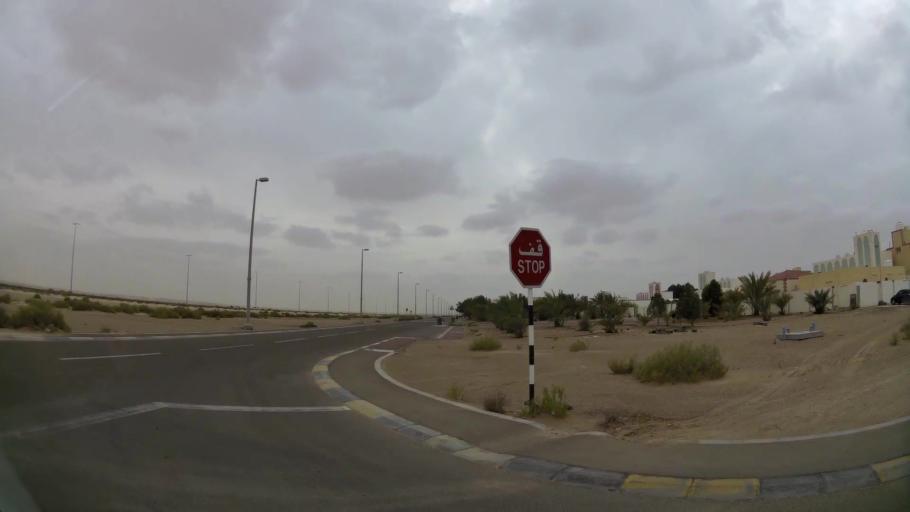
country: AE
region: Abu Dhabi
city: Abu Dhabi
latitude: 24.3556
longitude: 54.6633
